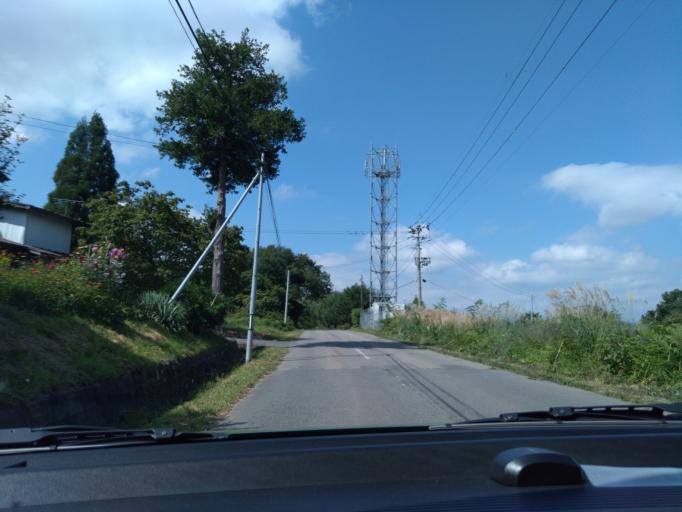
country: JP
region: Iwate
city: Shizukuishi
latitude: 39.6709
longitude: 140.9686
